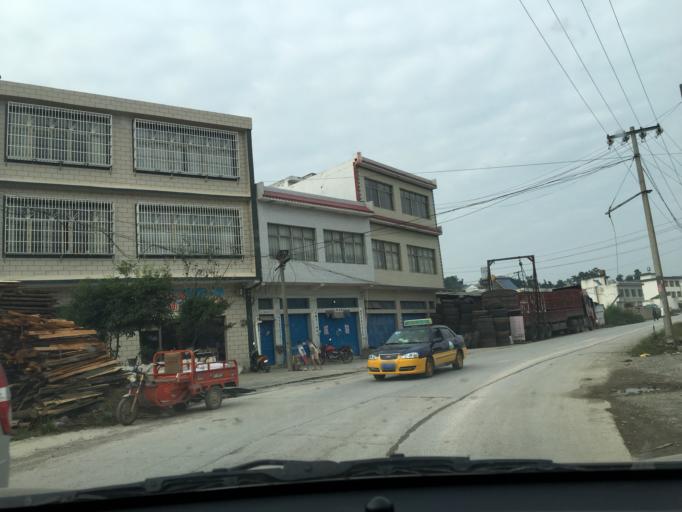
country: CN
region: Guangxi Zhuangzu Zizhiqu
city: Xinzhou
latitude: 25.4577
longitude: 105.4862
